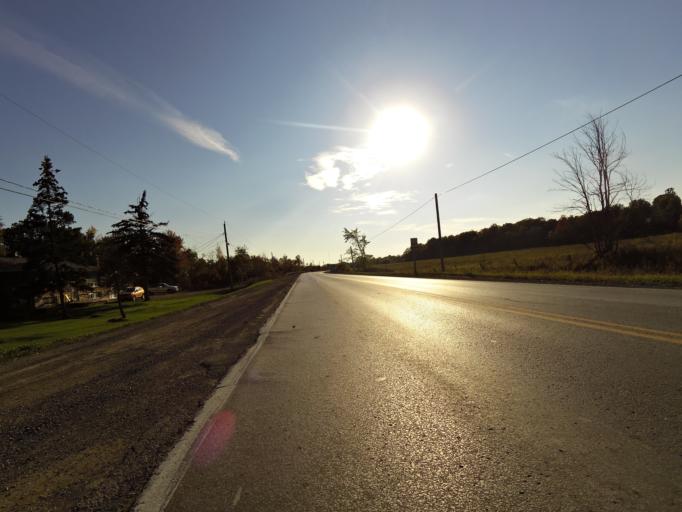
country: CA
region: Ontario
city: Kingston
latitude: 44.2820
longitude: -76.4692
